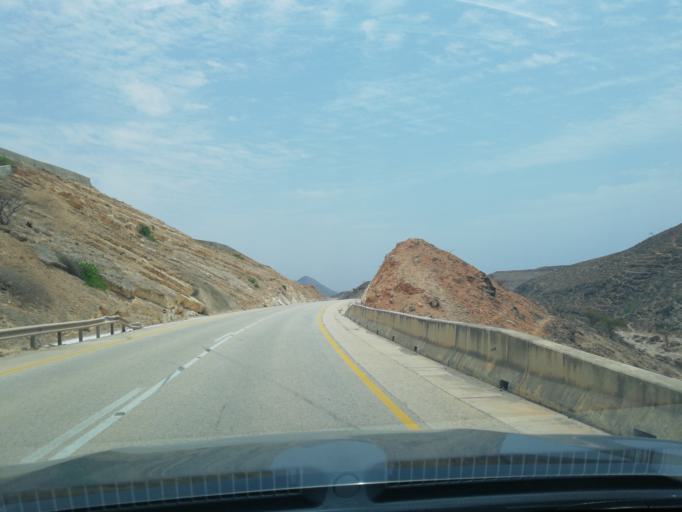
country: OM
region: Zufar
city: Salalah
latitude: 16.8788
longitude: 53.7347
